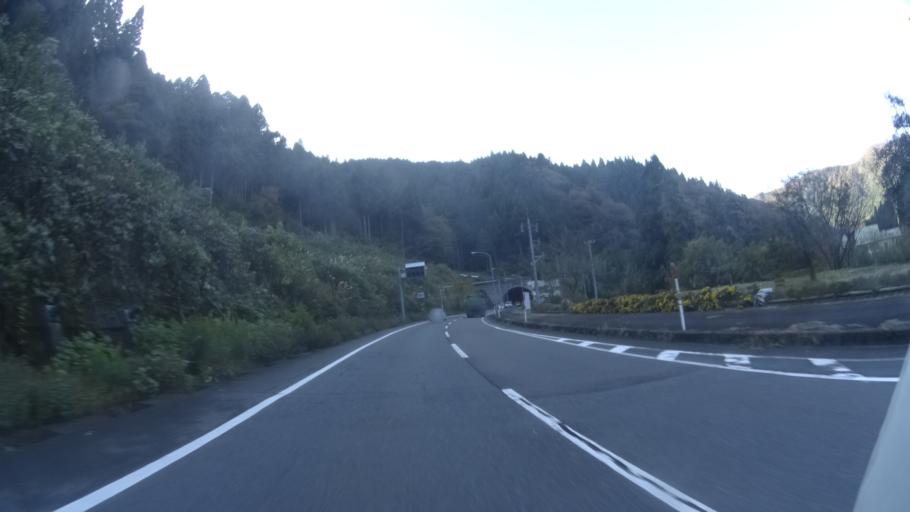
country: JP
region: Fukui
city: Ono
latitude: 36.0069
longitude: 136.3519
